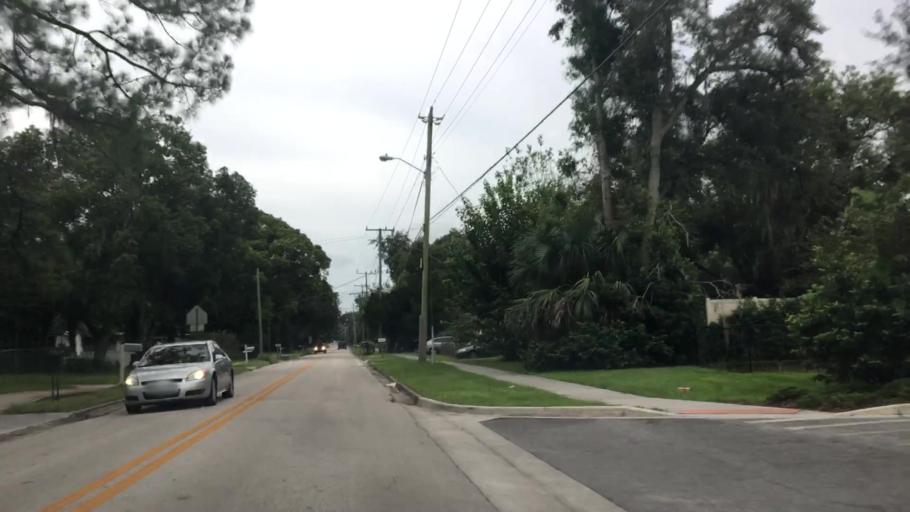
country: US
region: Florida
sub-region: Seminole County
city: Sanford
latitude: 28.8008
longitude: -81.2557
